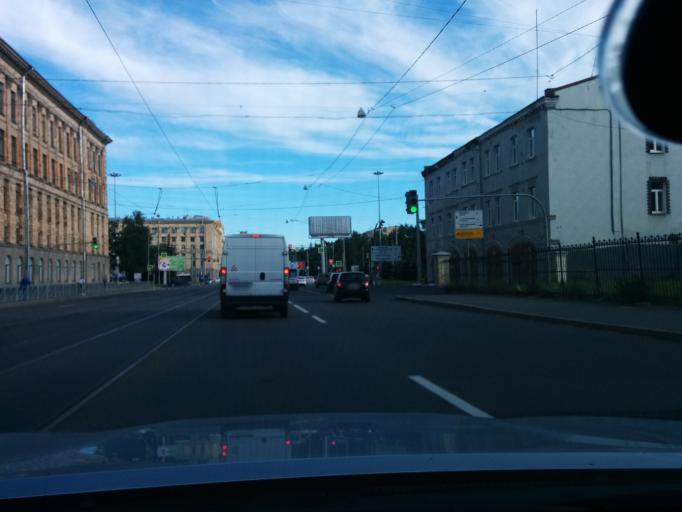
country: RU
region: Leningrad
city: Svetlanovskiy
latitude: 60.0050
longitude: 30.3270
